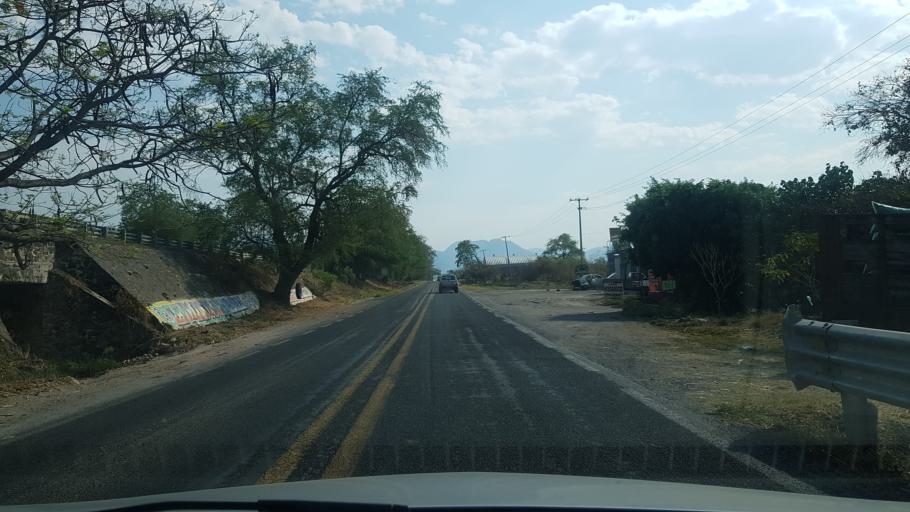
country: MX
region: Morelos
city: Puente de Ixtla
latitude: 18.6270
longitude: -99.3288
